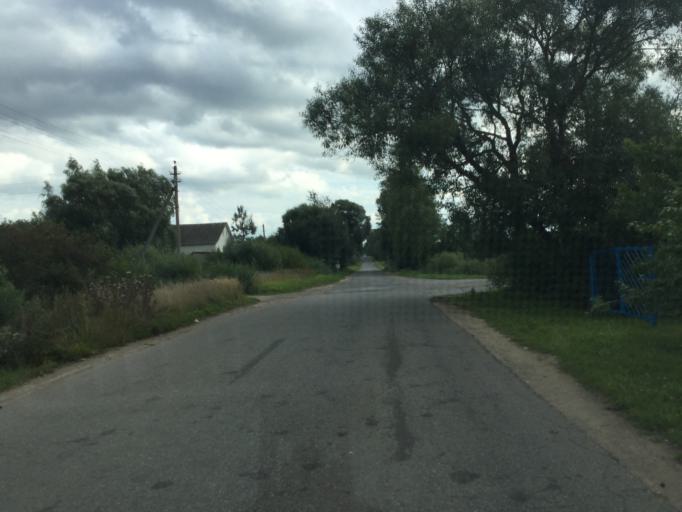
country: BY
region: Vitebsk
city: Vitebsk
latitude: 55.1489
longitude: 30.2785
